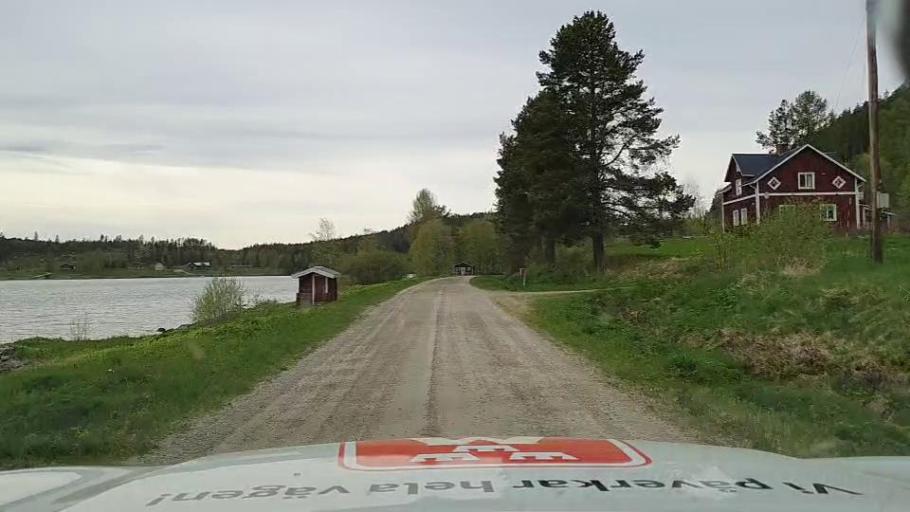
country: SE
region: Jaemtland
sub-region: Bergs Kommun
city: Hoverberg
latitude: 62.6859
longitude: 14.7885
